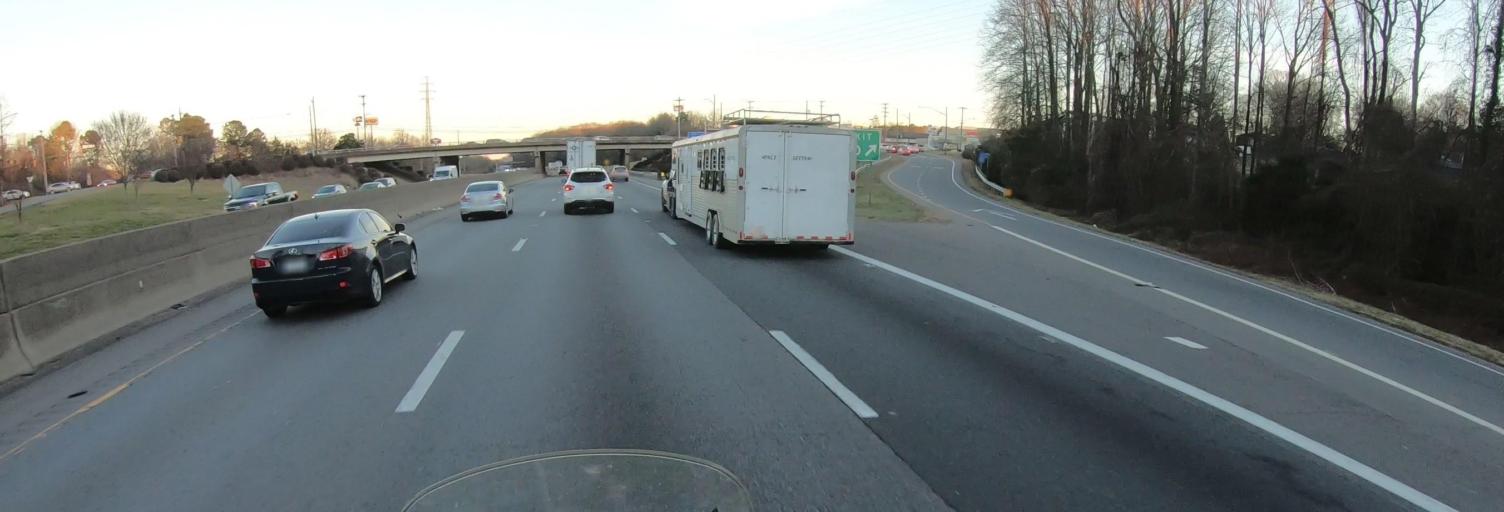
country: US
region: North Carolina
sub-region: Gaston County
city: Ranlo
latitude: 35.2701
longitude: -81.1501
